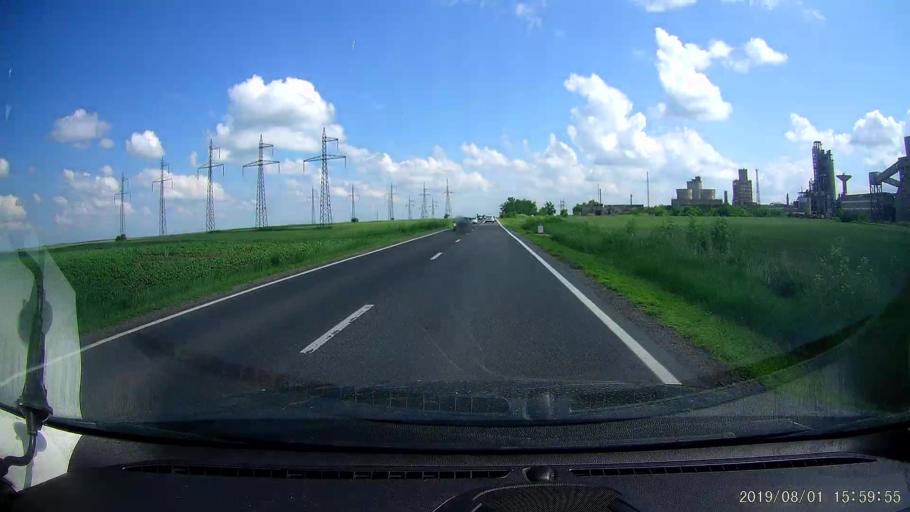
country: RO
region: Ialomita
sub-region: Comuna Slobozia
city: Slobozia
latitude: 44.5385
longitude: 27.3870
